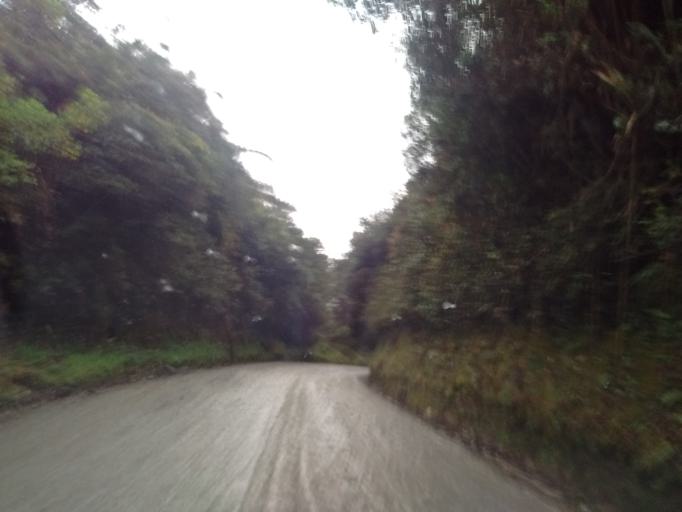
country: CO
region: Cauca
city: Paispamba
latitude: 2.1560
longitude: -76.4531
